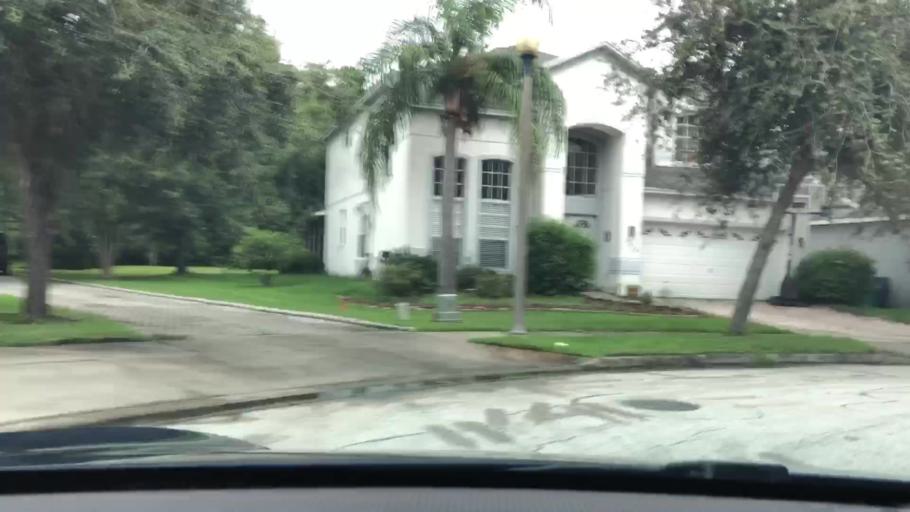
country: US
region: Florida
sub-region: Orange County
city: Conway
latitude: 28.4684
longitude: -81.2723
